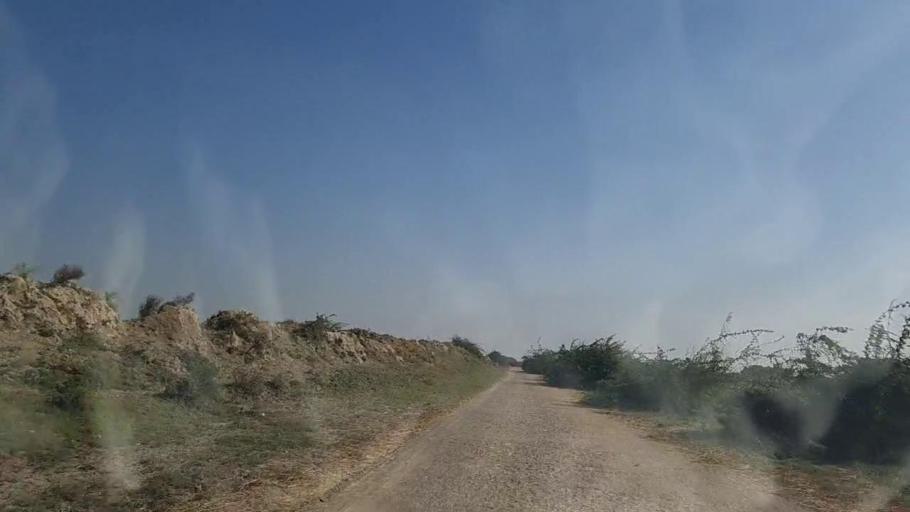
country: PK
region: Sindh
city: Mirpur Batoro
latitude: 24.6067
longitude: 68.1719
